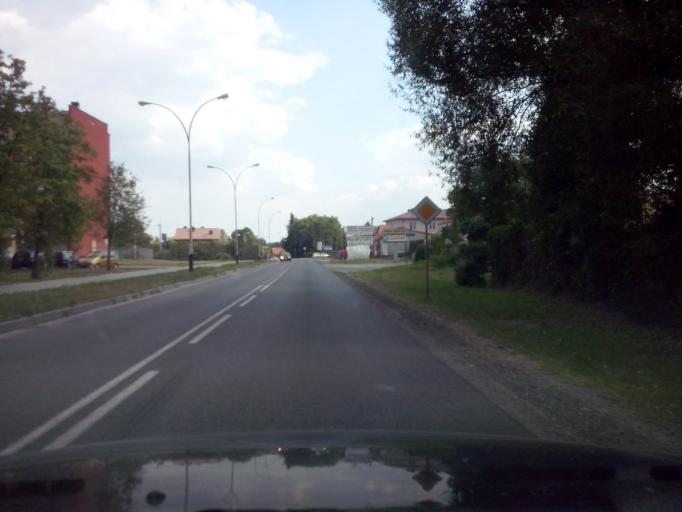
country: PL
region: Subcarpathian Voivodeship
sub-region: Powiat nizanski
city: Nisko
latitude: 50.5195
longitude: 22.1334
